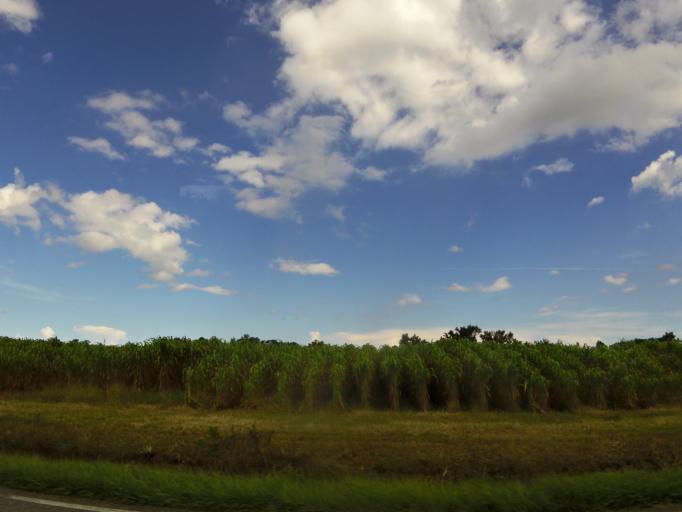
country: US
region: Florida
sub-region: Saint Johns County
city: Saint Augustine Shores
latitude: 29.7938
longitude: -81.4842
